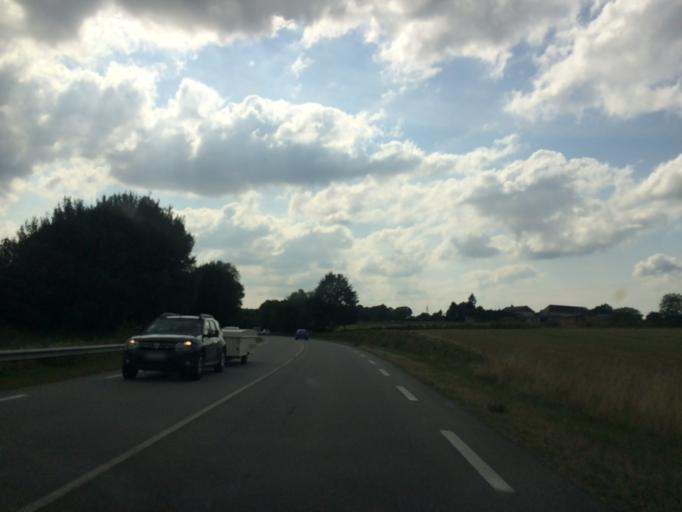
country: FR
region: Lower Normandy
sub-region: Departement de l'Orne
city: Tourouvre
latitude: 48.5667
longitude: 0.6220
